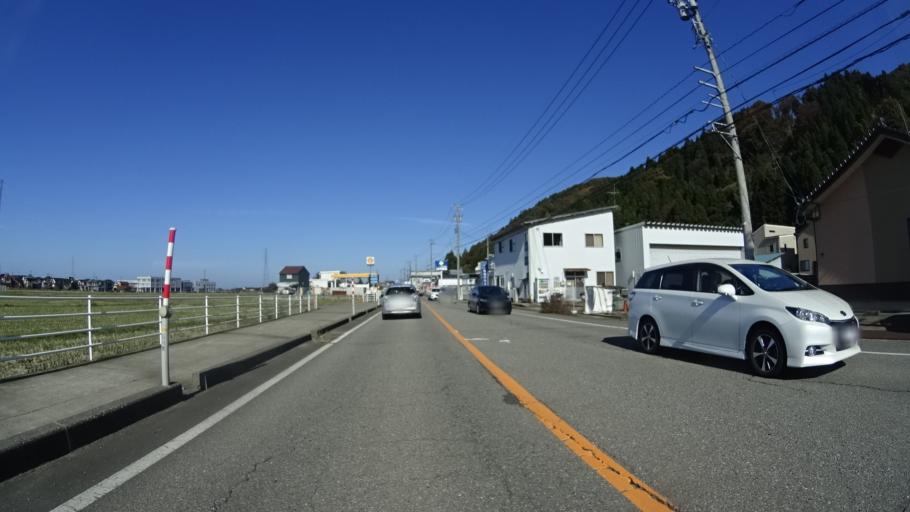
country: JP
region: Ishikawa
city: Tsurugi-asahimachi
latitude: 36.4654
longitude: 136.6195
